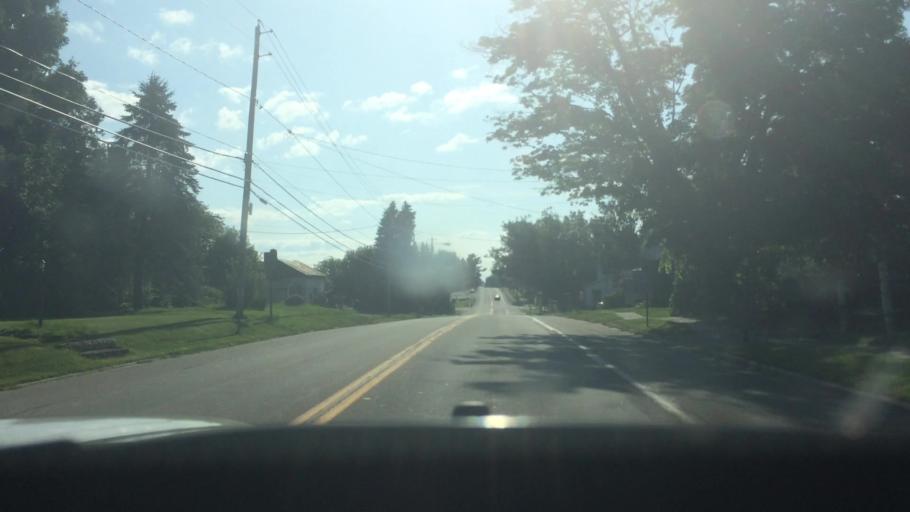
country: US
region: New York
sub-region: Franklin County
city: Malone
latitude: 44.8128
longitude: -74.3947
